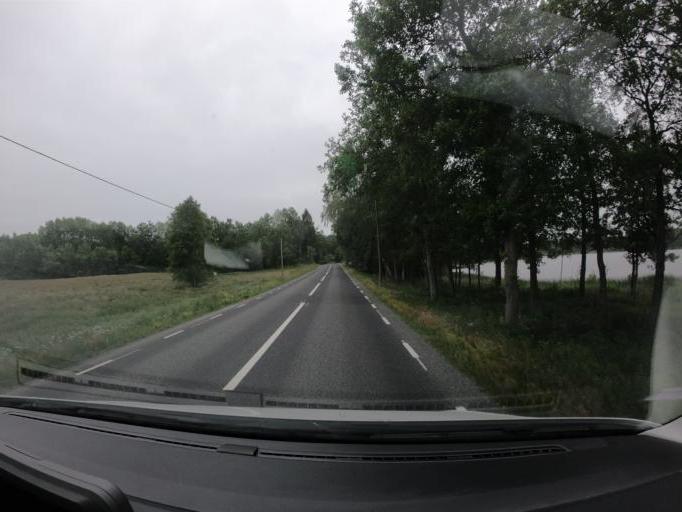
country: SE
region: Skane
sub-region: Orkelljunga Kommun
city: OErkelljunga
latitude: 56.2447
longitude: 13.3735
